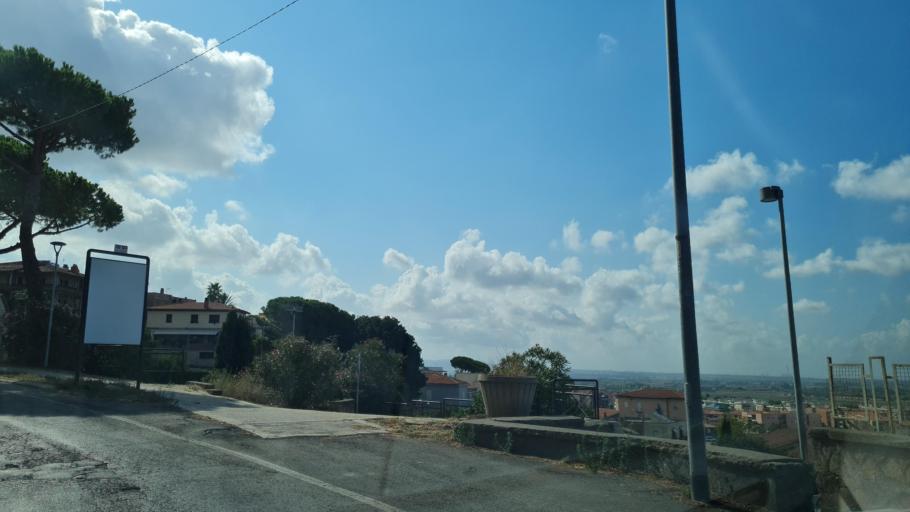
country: IT
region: Latium
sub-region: Provincia di Viterbo
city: Tarquinia
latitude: 42.2511
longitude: 11.7538
